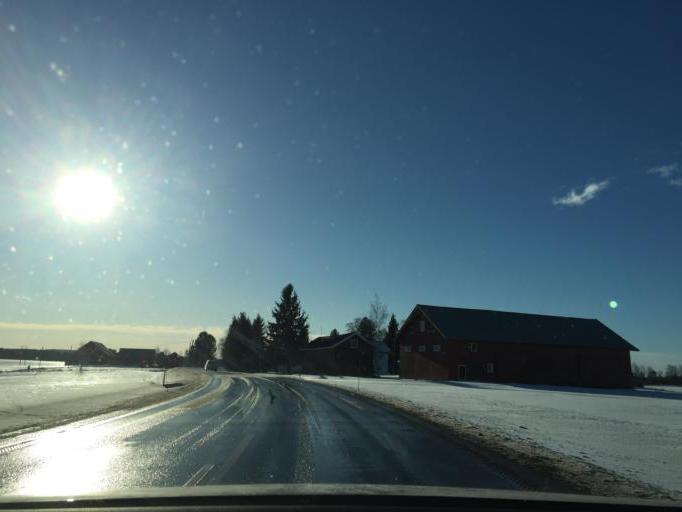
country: NO
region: Akershus
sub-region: Nes
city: Arnes
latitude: 60.1480
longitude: 11.4944
